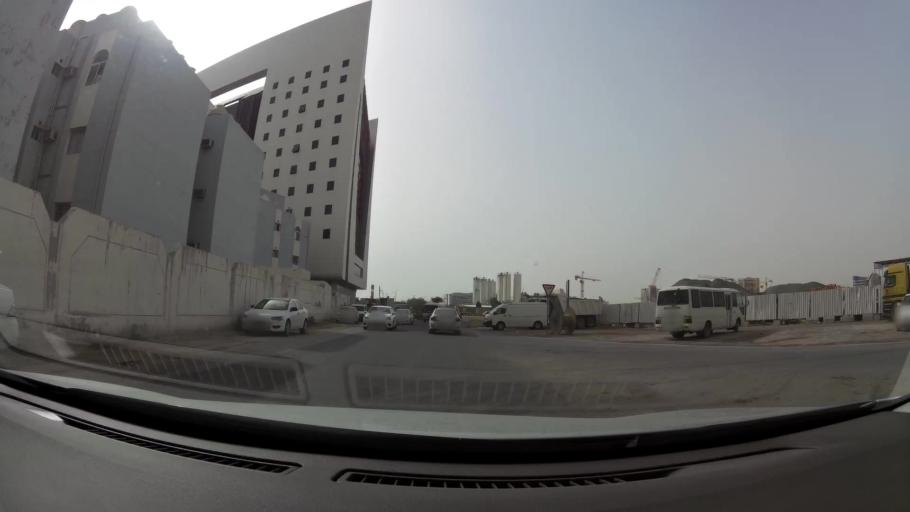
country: QA
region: Baladiyat ad Dawhah
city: Doha
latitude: 25.2749
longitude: 51.5509
